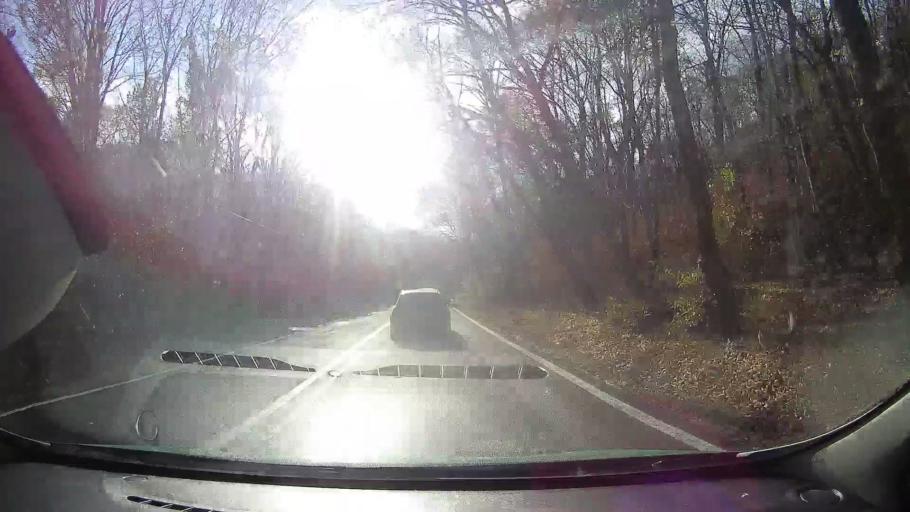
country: RO
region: Tulcea
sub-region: Comuna Ciucurova
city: Ciucurova
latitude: 44.9218
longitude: 28.4296
